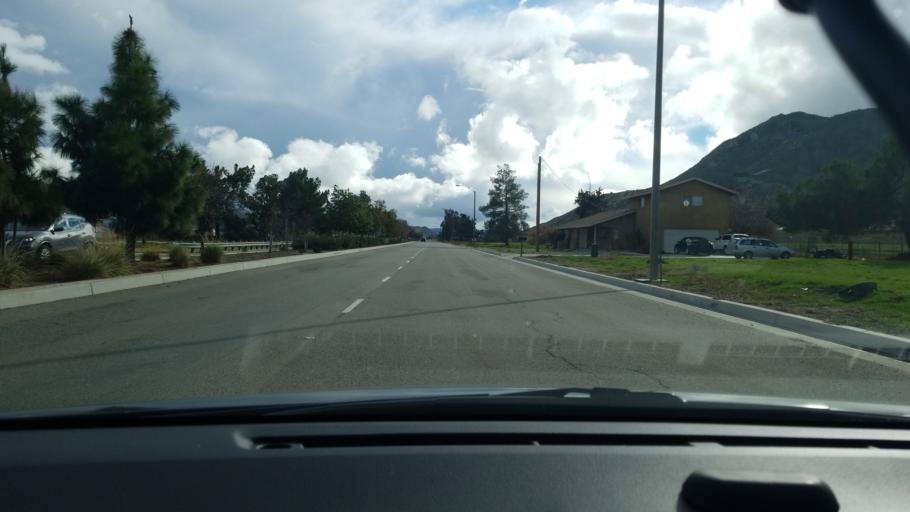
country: US
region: California
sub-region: Riverside County
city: Green Acres
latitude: 33.7958
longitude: -117.0338
